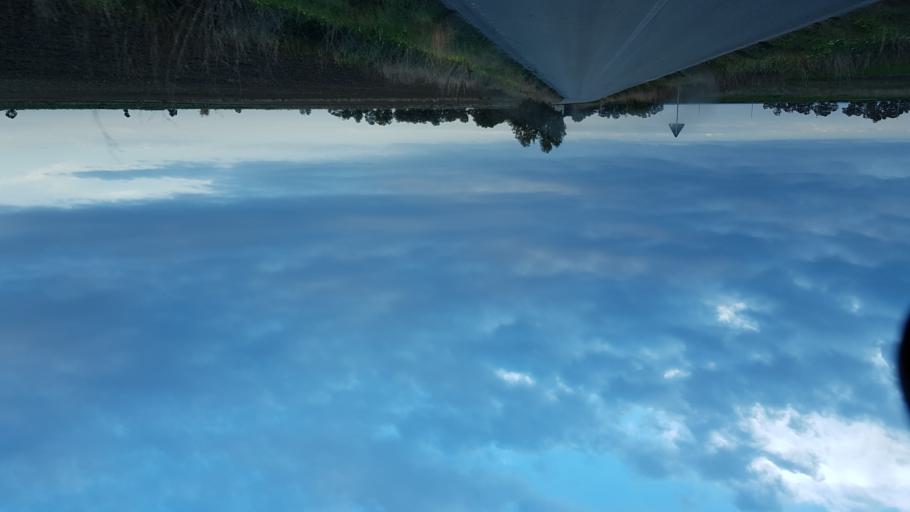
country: IT
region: Apulia
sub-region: Provincia di Brindisi
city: La Rosa
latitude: 40.5855
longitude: 18.0303
